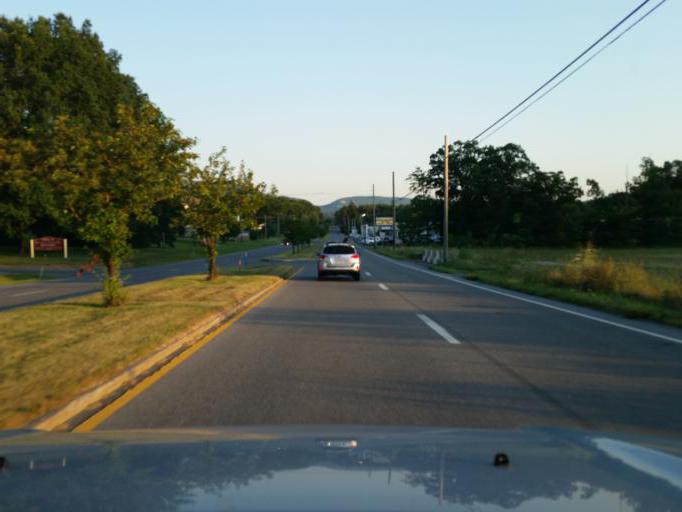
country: US
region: Pennsylvania
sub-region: Blair County
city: Lakemont
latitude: 40.4540
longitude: -78.3945
